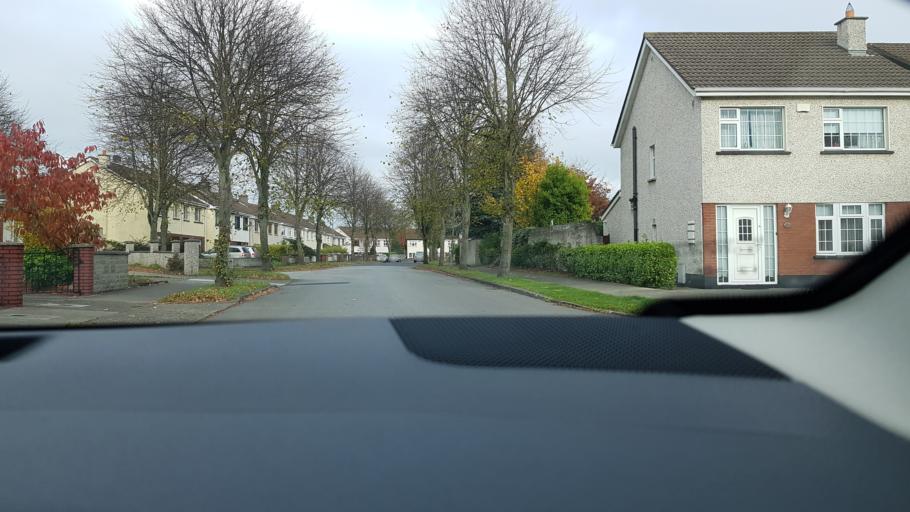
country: IE
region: Leinster
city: Hartstown
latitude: 53.3917
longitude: -6.4160
